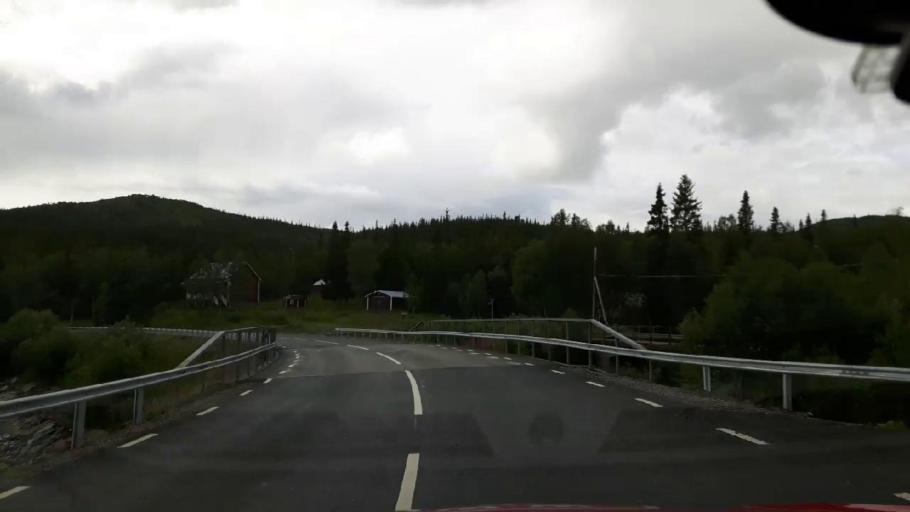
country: NO
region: Nord-Trondelag
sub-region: Royrvik
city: Royrvik
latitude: 64.8216
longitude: 14.0608
